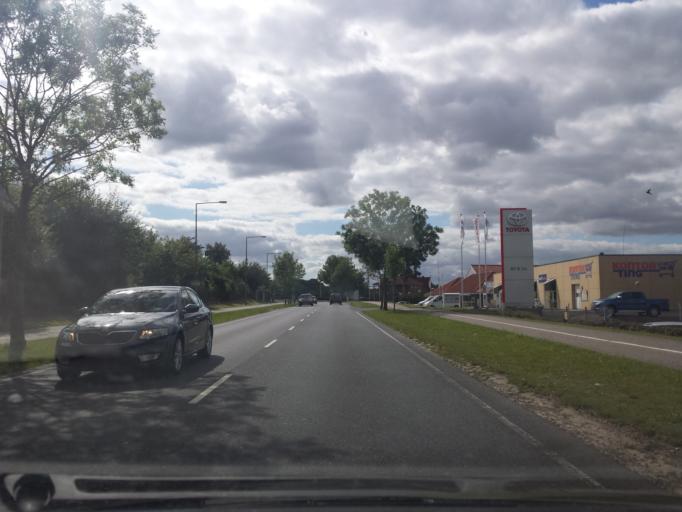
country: DK
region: South Denmark
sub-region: Sonderborg Kommune
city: Sonderborg
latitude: 54.9233
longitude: 9.7909
